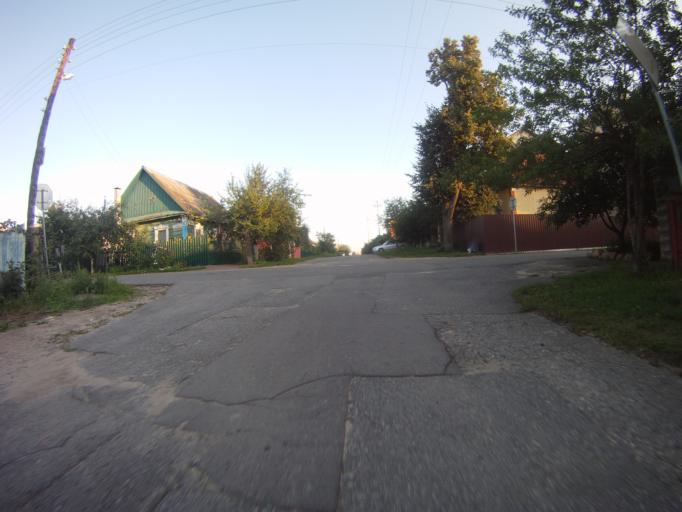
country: BY
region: Minsk
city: Minsk
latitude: 53.9397
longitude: 27.5592
